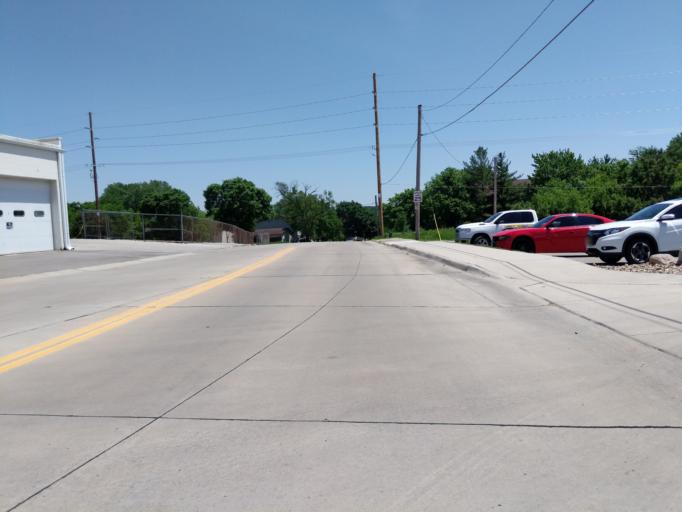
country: US
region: Iowa
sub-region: Linn County
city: Cedar Rapids
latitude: 42.0192
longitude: -91.6318
